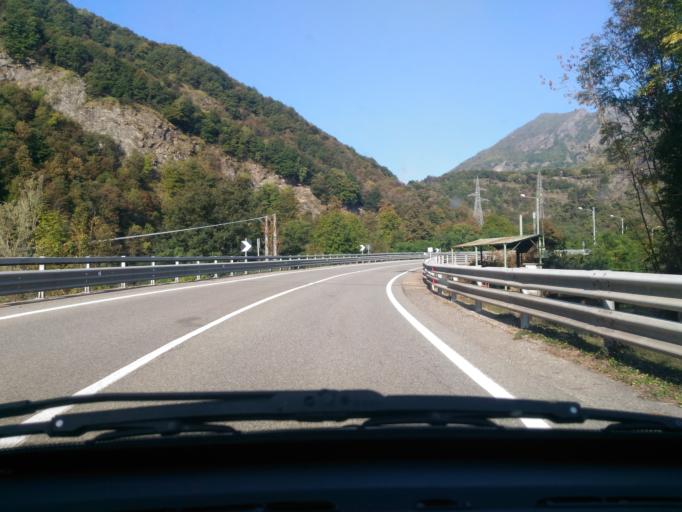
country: IT
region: Piedmont
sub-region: Provincia di Vercelli
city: Varallo
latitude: 45.8141
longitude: 8.2451
